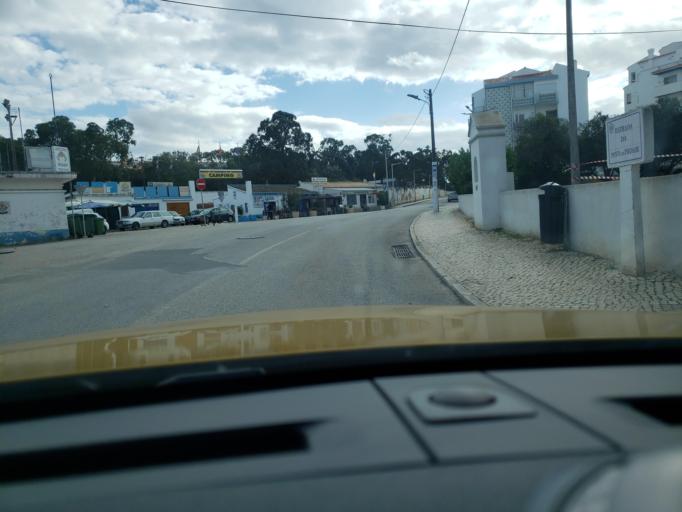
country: PT
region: Faro
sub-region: Lagos
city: Lagos
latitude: 37.0952
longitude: -8.6722
